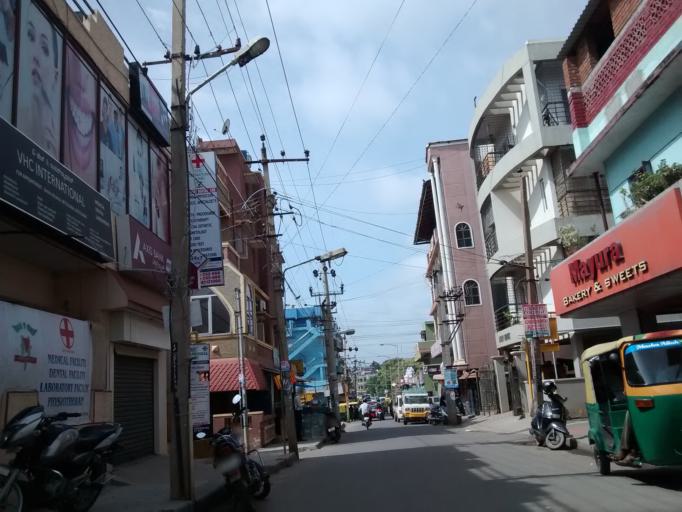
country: IN
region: Karnataka
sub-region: Bangalore Urban
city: Bangalore
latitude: 12.9682
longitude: 77.6701
